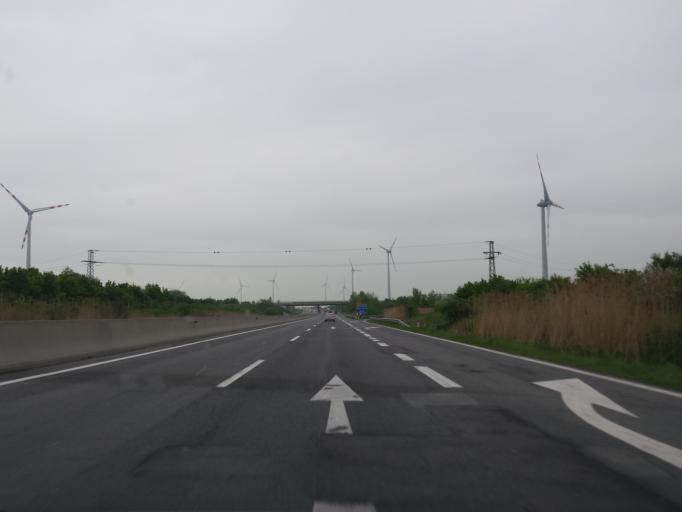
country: AT
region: Burgenland
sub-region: Politischer Bezirk Neusiedl am See
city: Zurndorf
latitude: 47.9300
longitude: 17.0007
